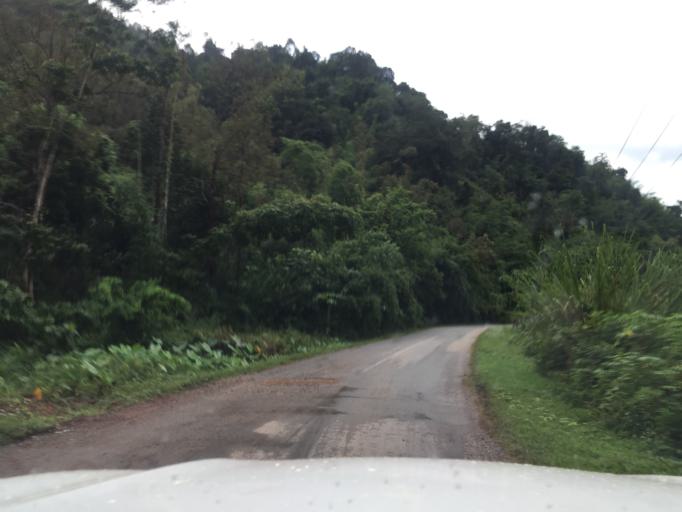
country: LA
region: Oudomxai
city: Muang La
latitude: 20.8229
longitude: 102.0965
